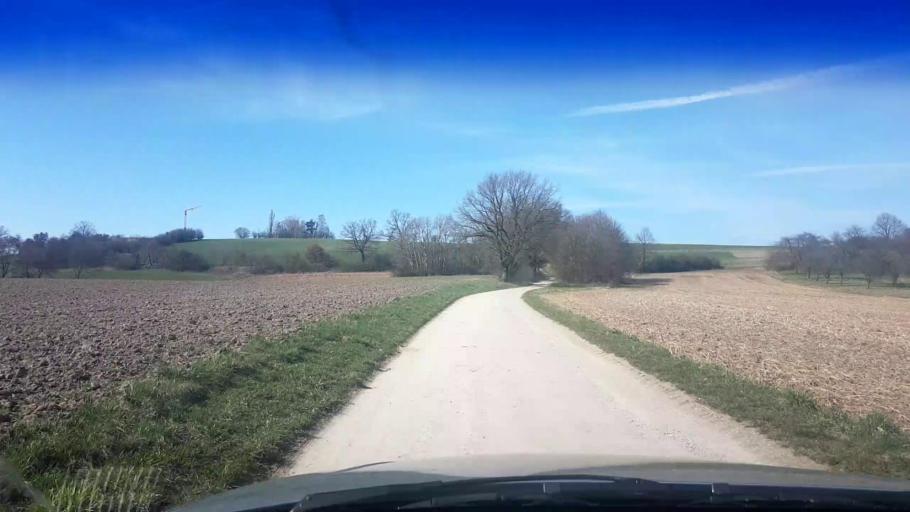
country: DE
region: Bavaria
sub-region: Upper Franconia
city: Bischberg
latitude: 49.8971
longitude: 10.8269
